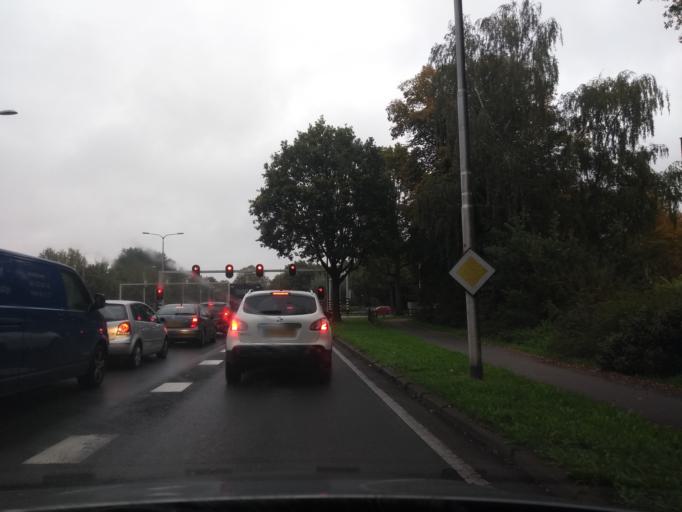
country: NL
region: Overijssel
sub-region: Gemeente Almelo
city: Almelo
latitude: 52.3665
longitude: 6.6717
